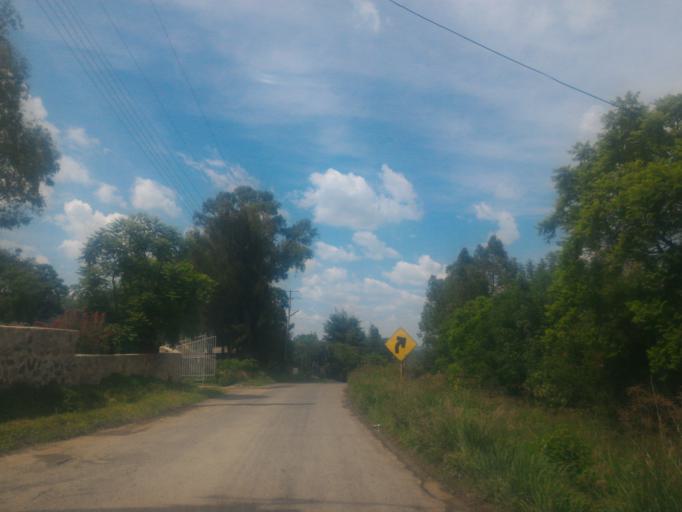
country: MX
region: Guanajuato
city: Ciudad Manuel Doblado
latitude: 20.8245
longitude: -102.0580
